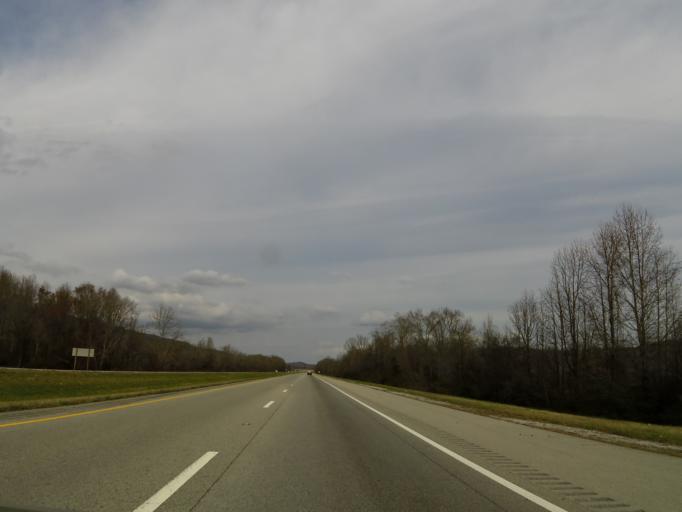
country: US
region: Tennessee
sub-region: Hamilton County
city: Soddy-Daisy
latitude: 35.2218
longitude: -85.2089
